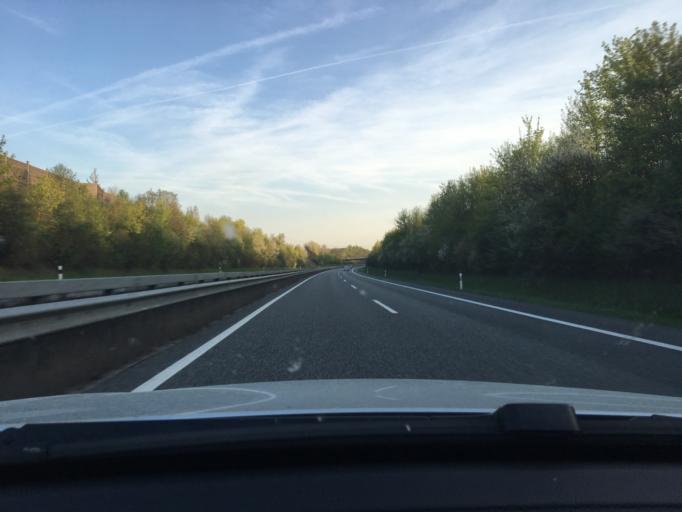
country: DE
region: Rheinland-Pfalz
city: Marnheim
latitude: 49.6340
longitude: 8.0335
